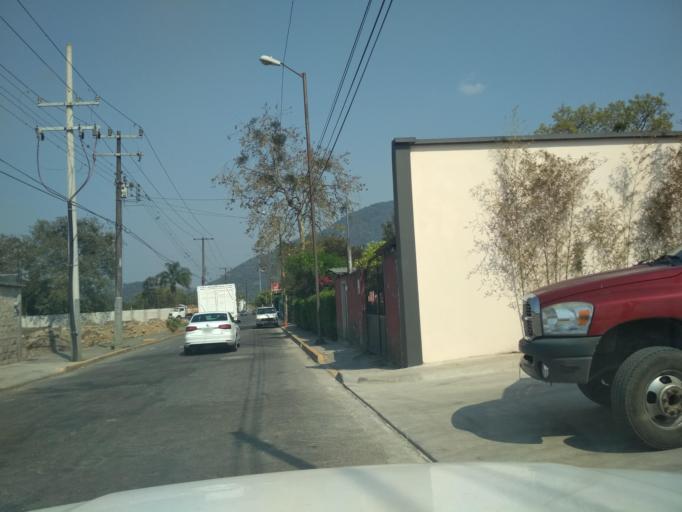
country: MX
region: Veracruz
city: Jalapilla
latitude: 18.8362
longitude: -97.0849
